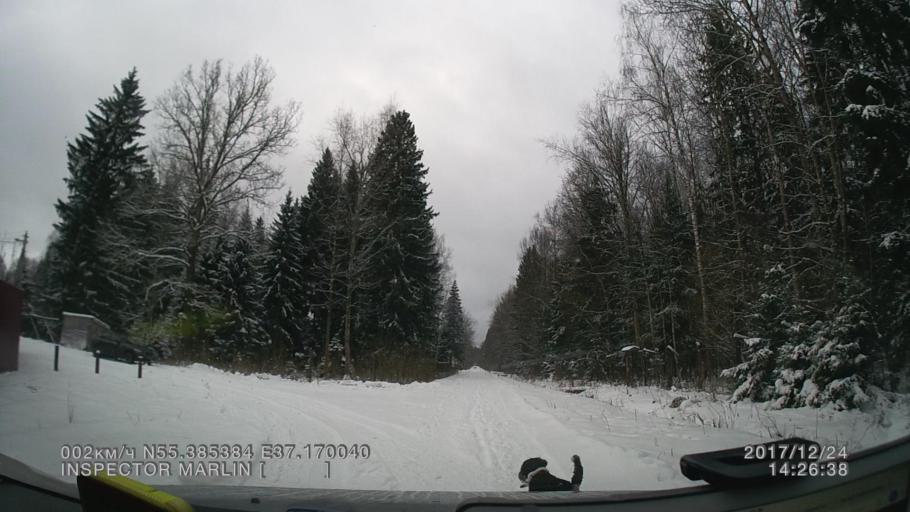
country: RU
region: Moskovskaya
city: Troitsk
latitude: 55.3853
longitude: 37.1699
